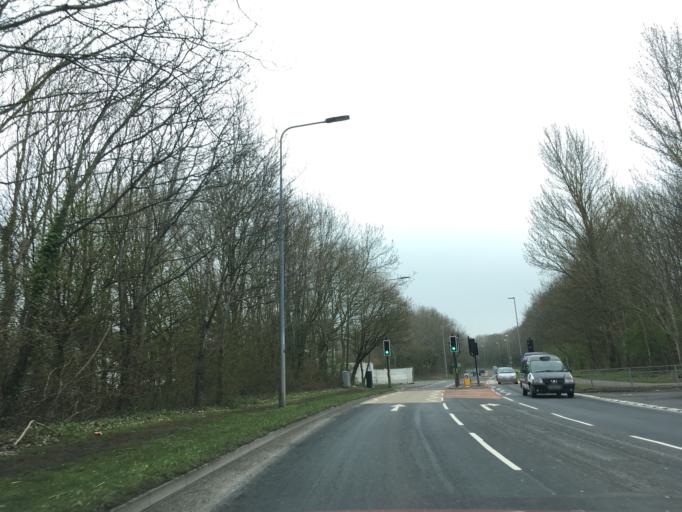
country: GB
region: Wales
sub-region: Newport
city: Newport
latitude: 51.5561
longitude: -3.0256
